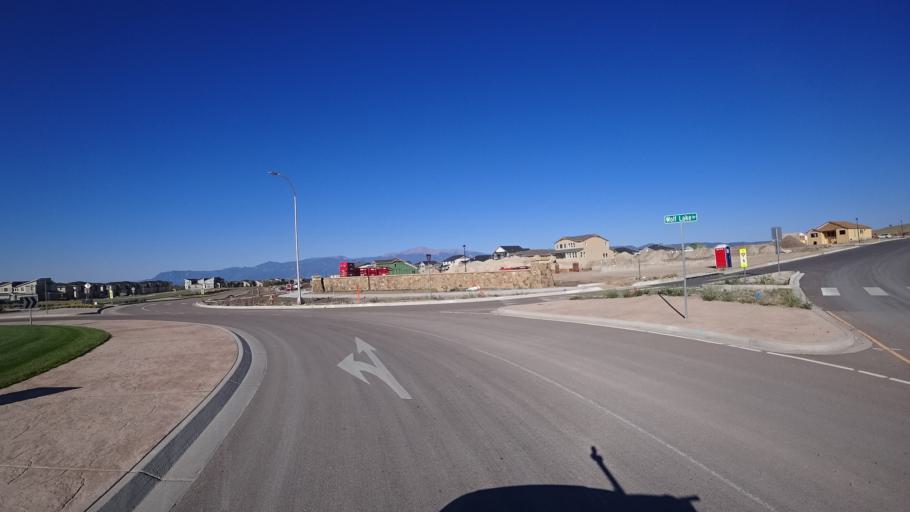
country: US
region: Colorado
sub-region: El Paso County
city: Black Forest
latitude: 38.9755
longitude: -104.7166
